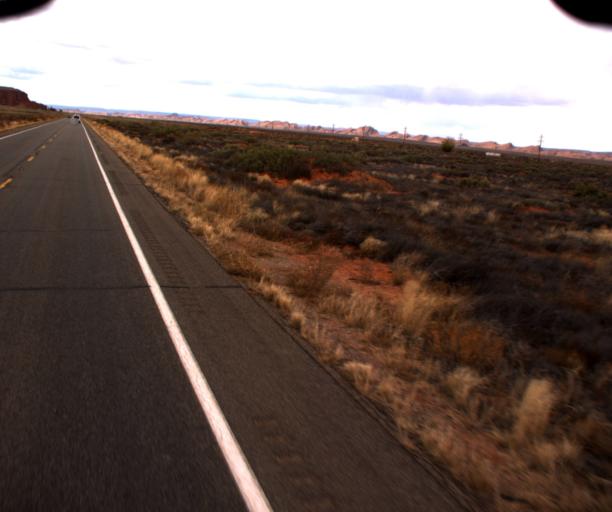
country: US
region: Arizona
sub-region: Navajo County
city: Kayenta
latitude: 36.7821
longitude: -109.9832
